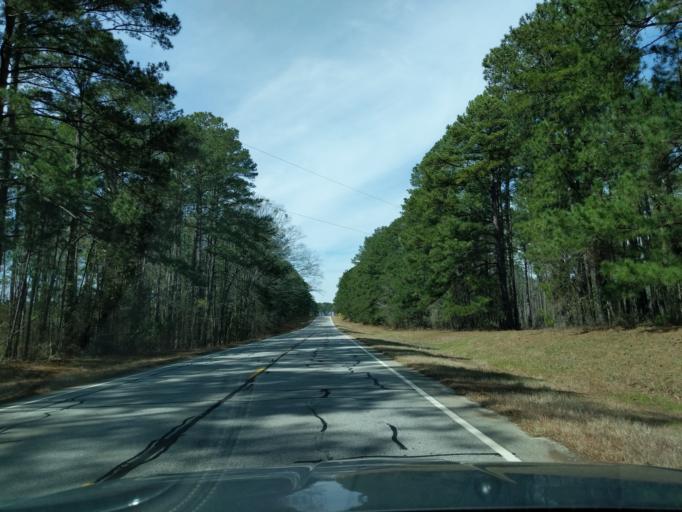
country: US
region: Georgia
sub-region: Columbia County
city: Appling
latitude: 33.6525
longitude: -82.2301
